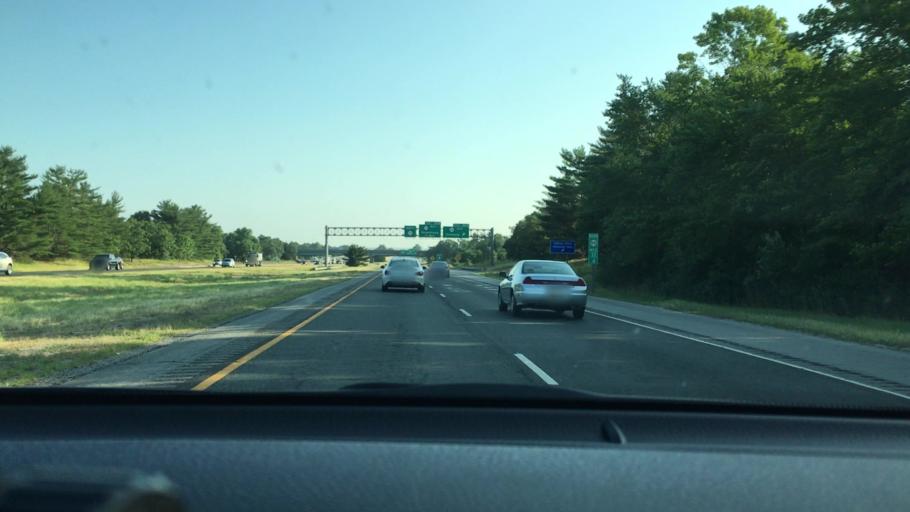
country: US
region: New Jersey
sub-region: Cumberland County
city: Vineland
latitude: 39.4840
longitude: -75.0717
